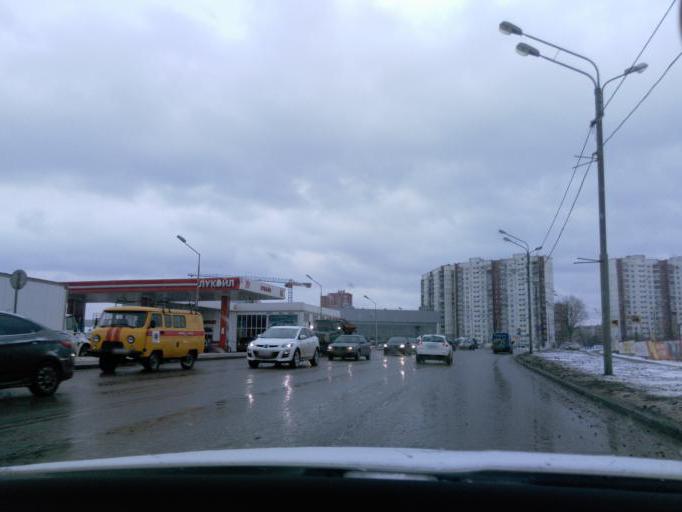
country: RU
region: Moscow
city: Khimki
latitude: 55.9095
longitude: 37.4066
